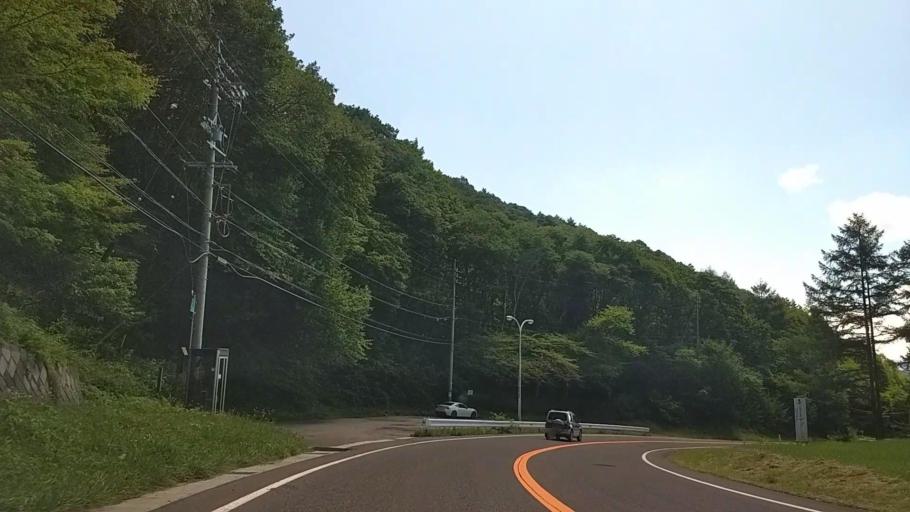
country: JP
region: Nagano
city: Chino
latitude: 36.0848
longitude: 138.2232
